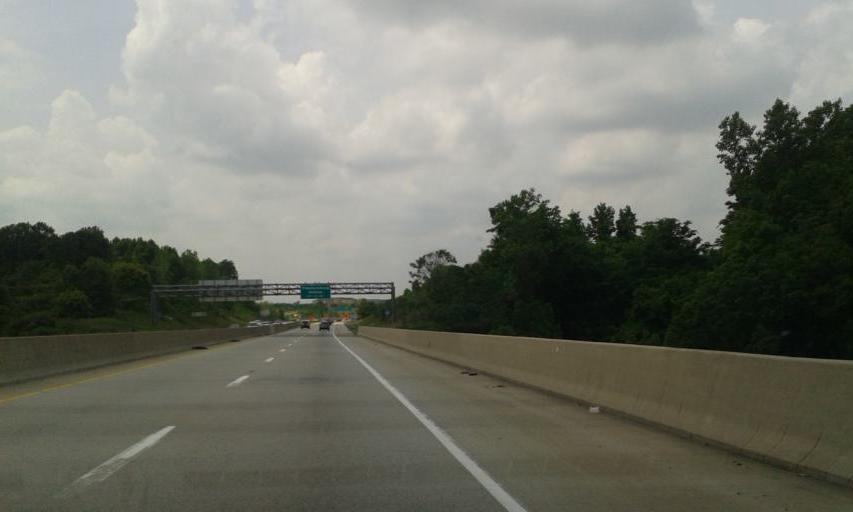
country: US
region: Pennsylvania
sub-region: Northampton County
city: Old Orchard
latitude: 40.6433
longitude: -75.2782
